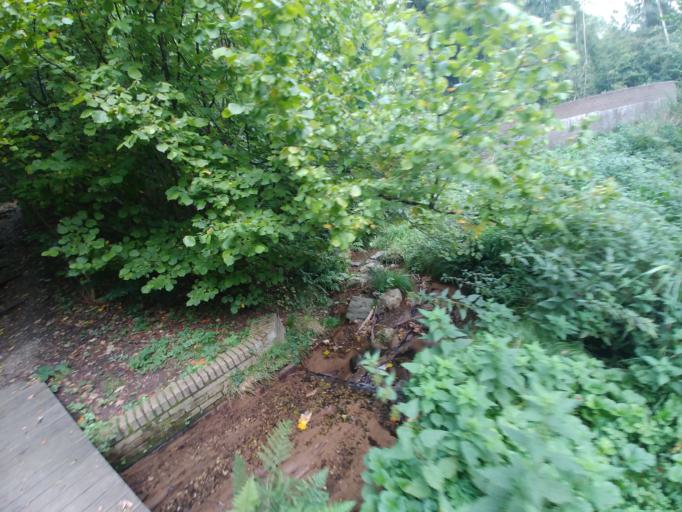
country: NL
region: Gelderland
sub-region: Gemeente Overbetuwe
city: Driel
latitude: 51.9745
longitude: 5.8151
